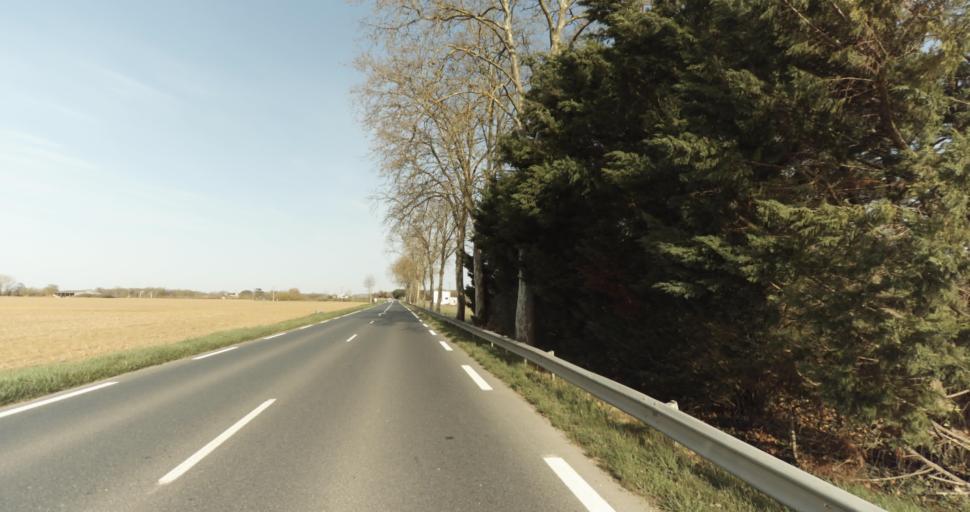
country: FR
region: Midi-Pyrenees
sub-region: Departement du Tarn
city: Saint-Sulpice-la-Pointe
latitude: 43.7565
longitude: 1.7159
